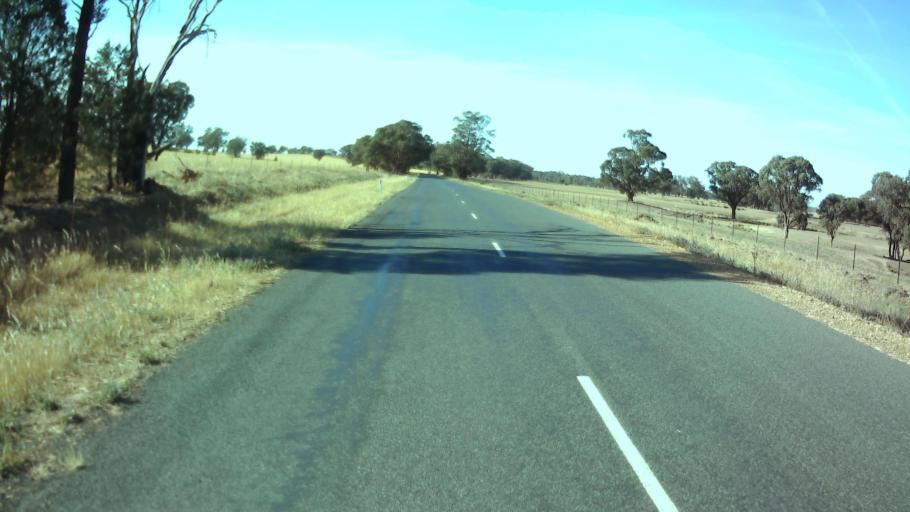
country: AU
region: New South Wales
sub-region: Weddin
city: Grenfell
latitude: -33.9719
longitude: 148.1408
